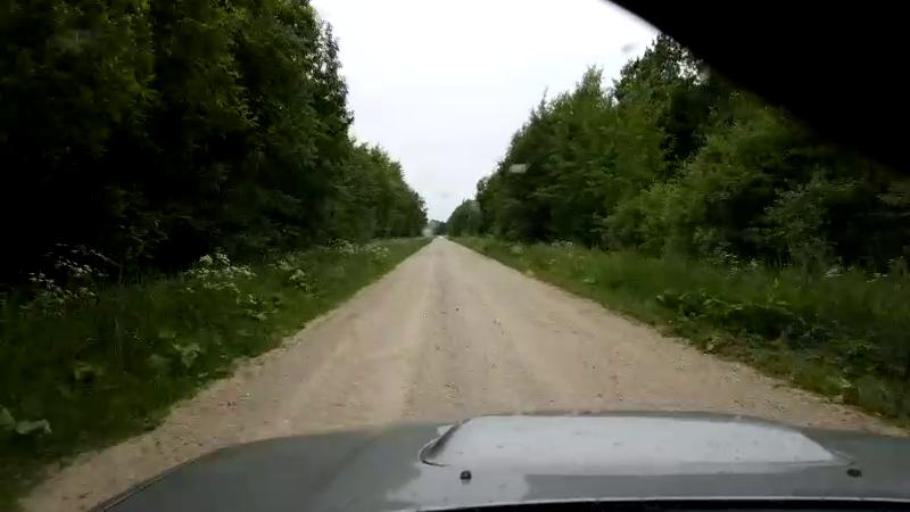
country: EE
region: Paernumaa
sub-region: Halinga vald
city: Parnu-Jaagupi
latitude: 58.5359
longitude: 24.5932
